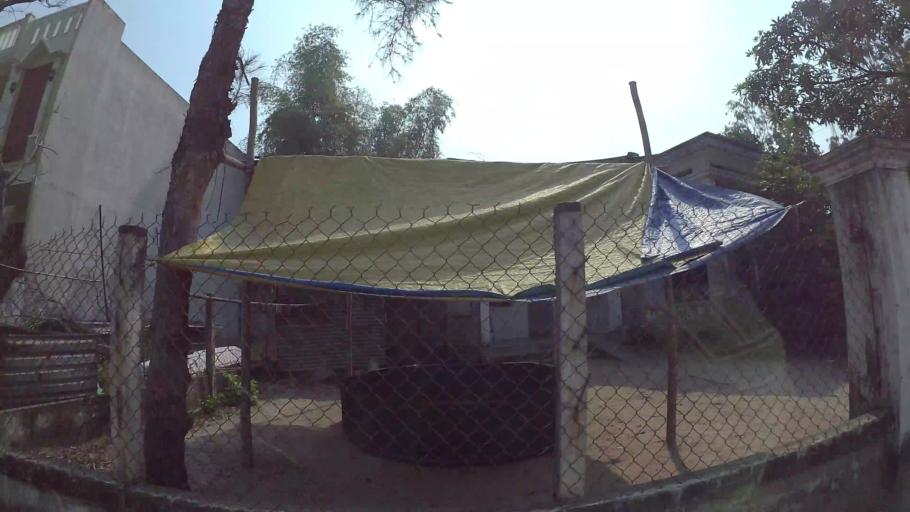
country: VN
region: Da Nang
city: Ngu Hanh Son
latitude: 15.9893
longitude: 108.2415
